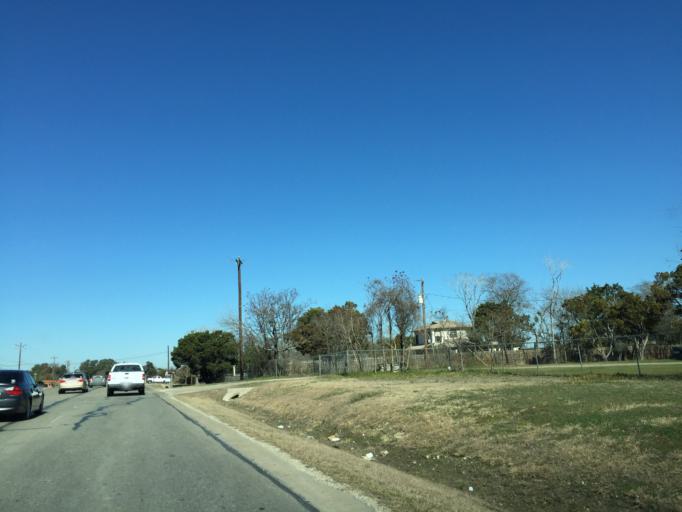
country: US
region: Texas
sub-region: Williamson County
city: Leander
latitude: 30.5629
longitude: -97.8633
